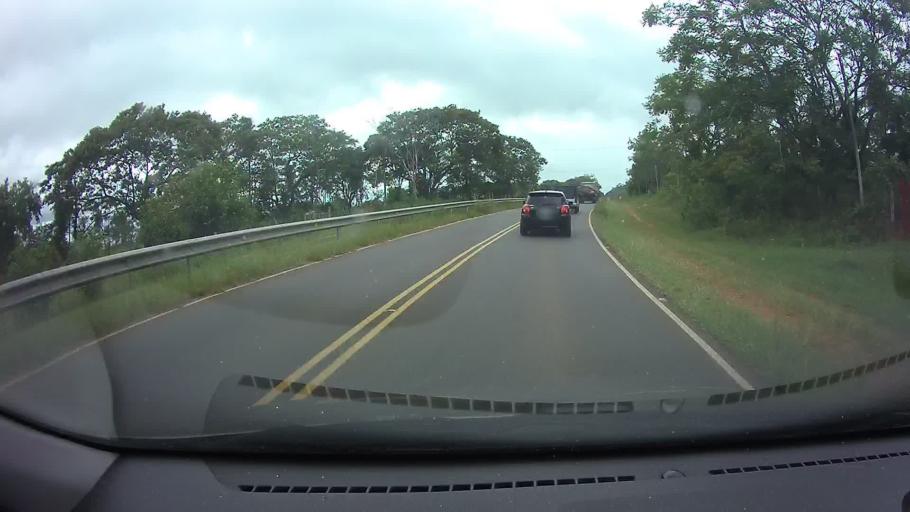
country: PY
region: Paraguari
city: Carapegua
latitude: -25.7391
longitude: -57.2860
